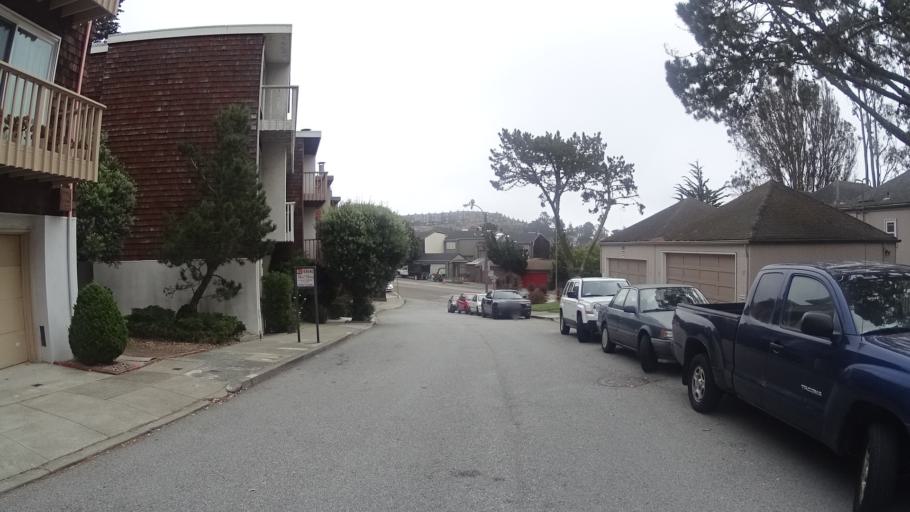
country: US
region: California
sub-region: San Francisco County
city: San Francisco
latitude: 37.7388
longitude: -122.4374
